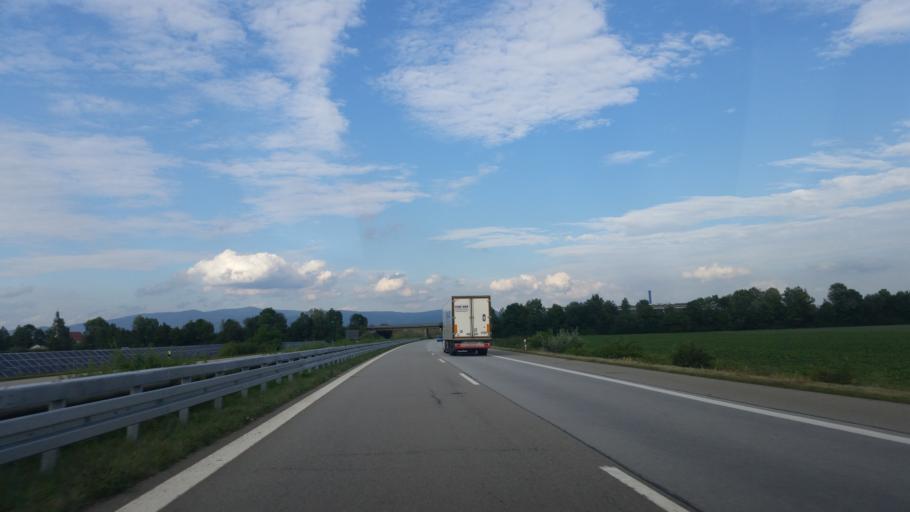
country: DE
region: Bavaria
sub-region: Lower Bavaria
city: Plattling
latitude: 48.7980
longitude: 12.8472
